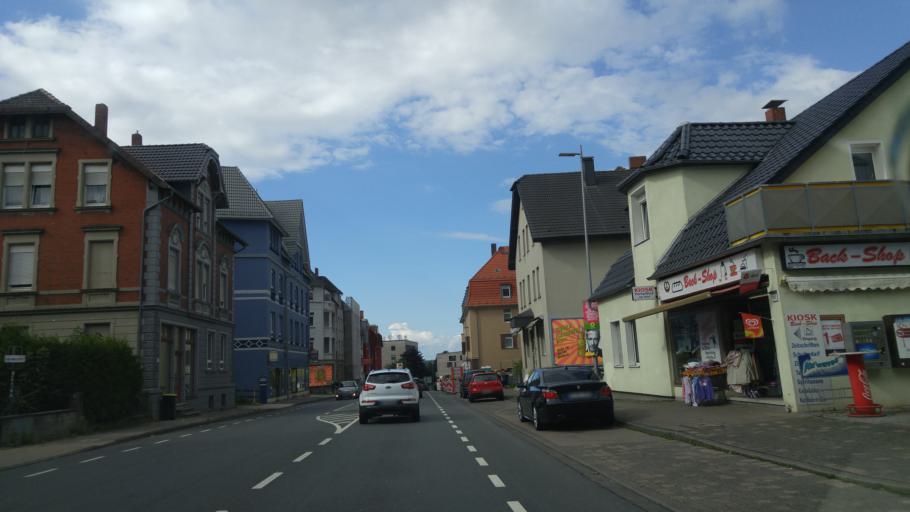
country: DE
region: North Rhine-Westphalia
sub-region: Regierungsbezirk Detmold
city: Bielefeld
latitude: 52.0348
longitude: 8.5240
